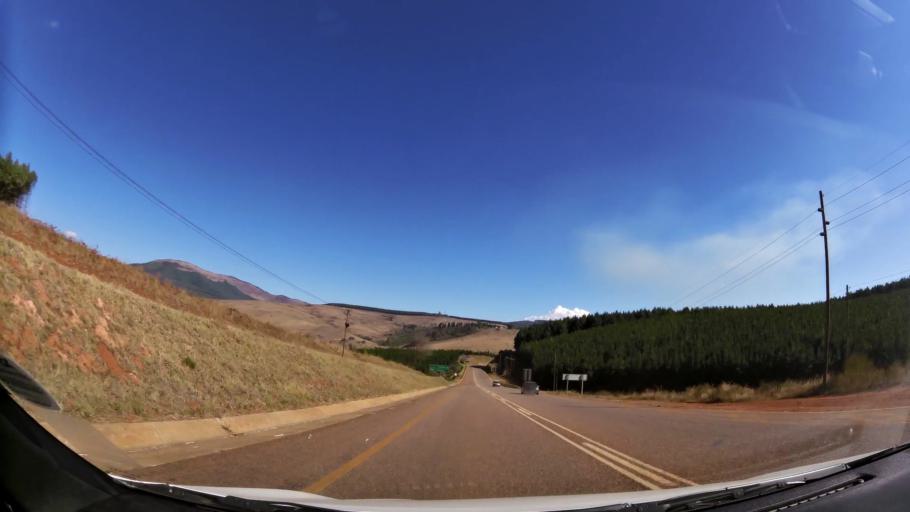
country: ZA
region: Limpopo
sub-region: Capricorn District Municipality
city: Mankoeng
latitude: -23.9363
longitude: 29.9527
